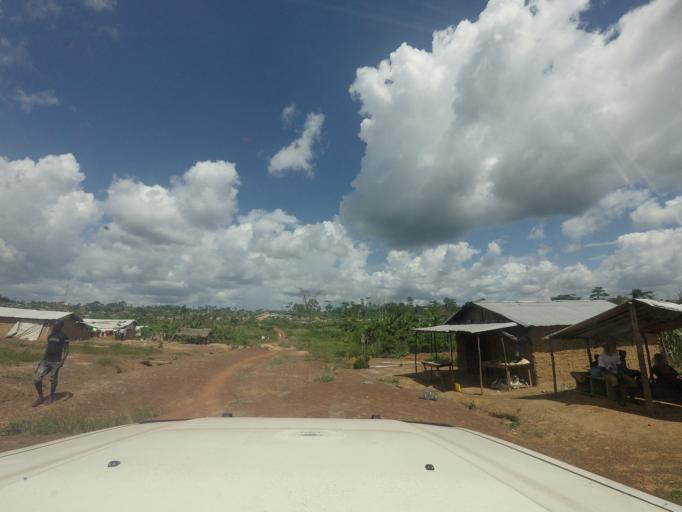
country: LR
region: Grand Gedeh
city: Zwedru
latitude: 6.0324
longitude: -8.0549
